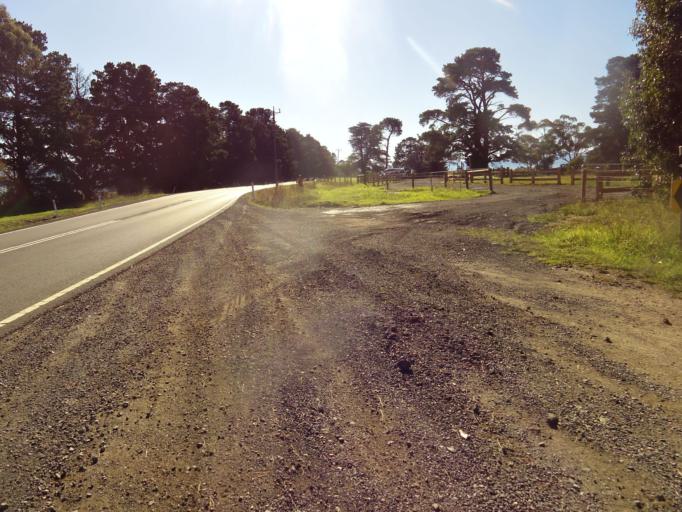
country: AU
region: Victoria
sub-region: Yarra Ranges
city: Yarra Glen
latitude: -37.6946
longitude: 145.3734
